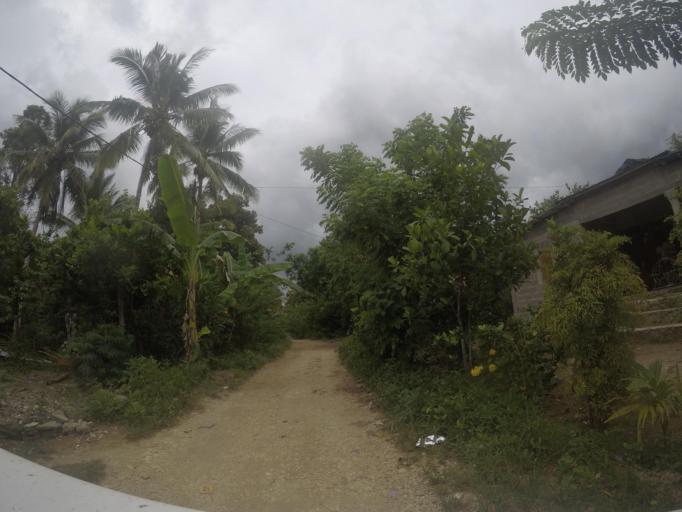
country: TL
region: Lautem
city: Lospalos
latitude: -8.5244
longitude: 126.9922
